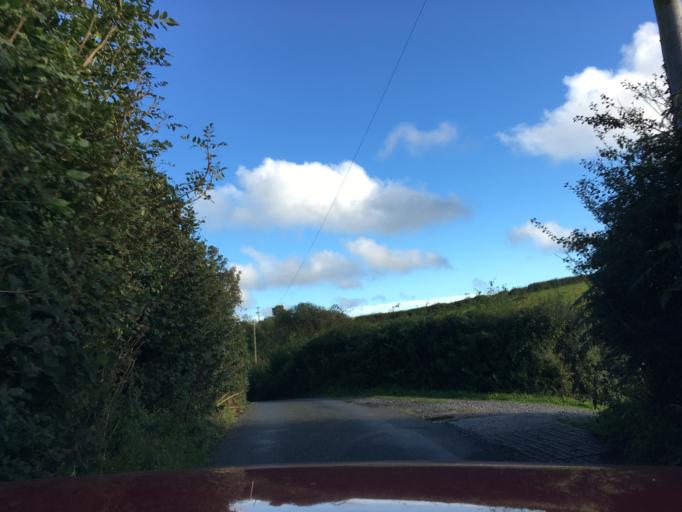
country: GB
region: England
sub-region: Devon
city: Dartmouth
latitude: 50.3334
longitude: -3.6015
